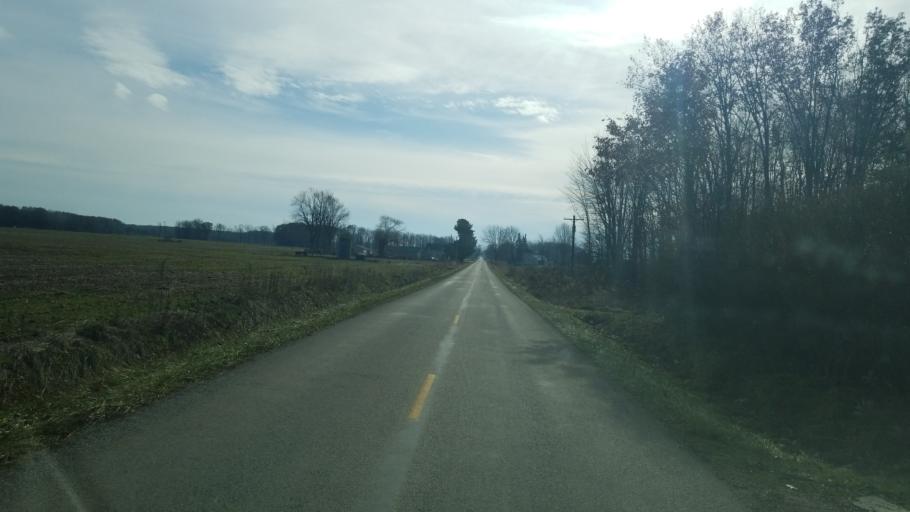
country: US
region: Ohio
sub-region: Ashtabula County
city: Roaming Shores
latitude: 41.6384
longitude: -80.7218
